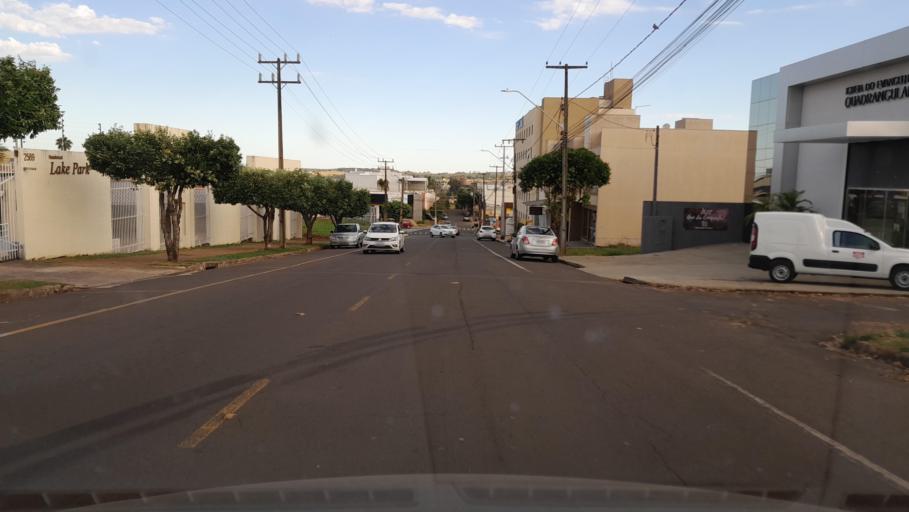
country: BR
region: Parana
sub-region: Umuarama
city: Umuarama
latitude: -23.7536
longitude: -53.2833
